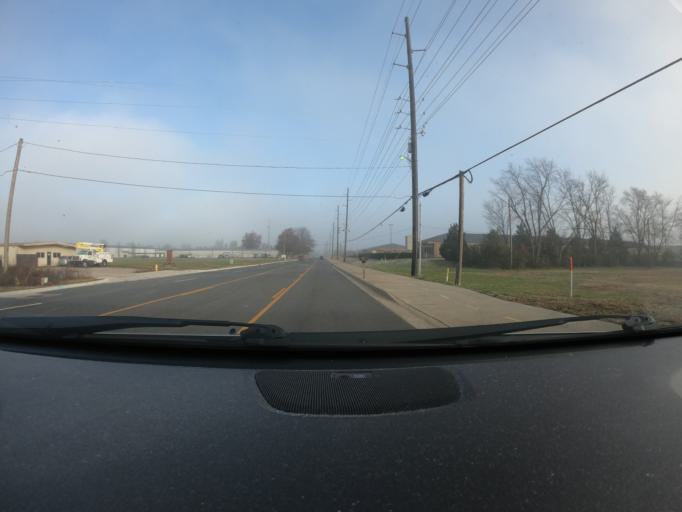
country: US
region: Arkansas
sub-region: Benton County
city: Bentonville
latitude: 36.3595
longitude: -94.2219
